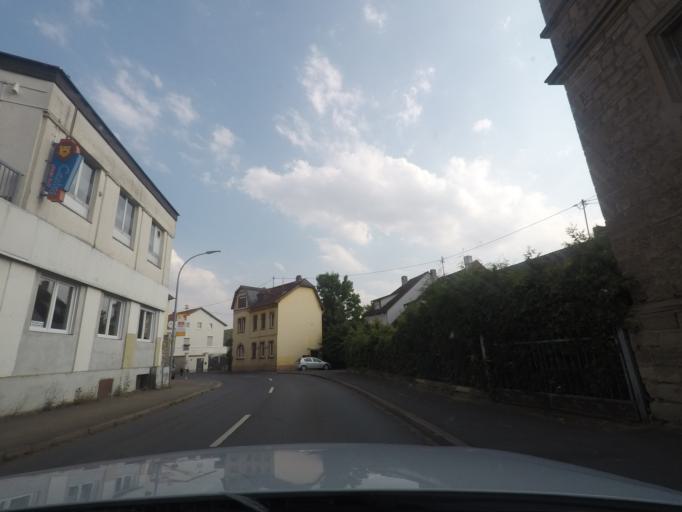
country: DE
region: Rheinland-Pfalz
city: Meddersheim
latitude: 49.7848
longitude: 7.6480
